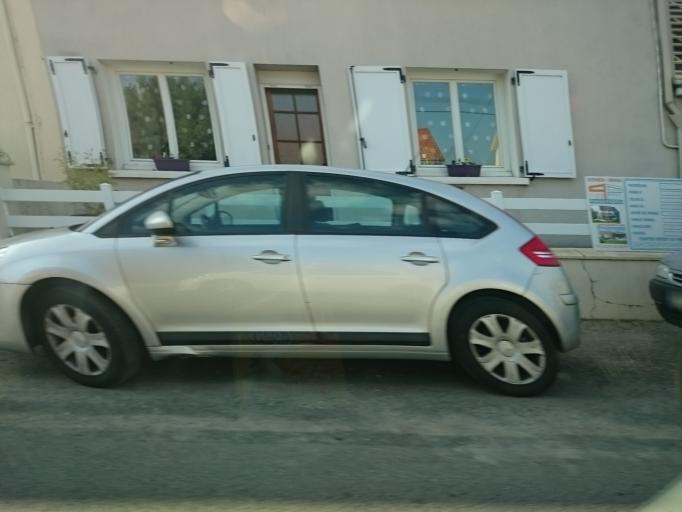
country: FR
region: Pays de la Loire
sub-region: Departement de la Loire-Atlantique
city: La Montagne
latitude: 47.1870
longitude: -1.6911
